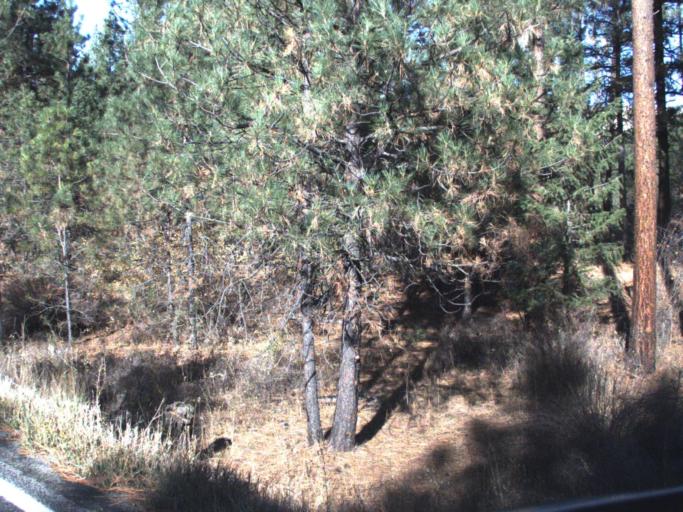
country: US
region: Washington
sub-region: Lincoln County
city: Davenport
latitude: 48.0799
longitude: -118.2000
